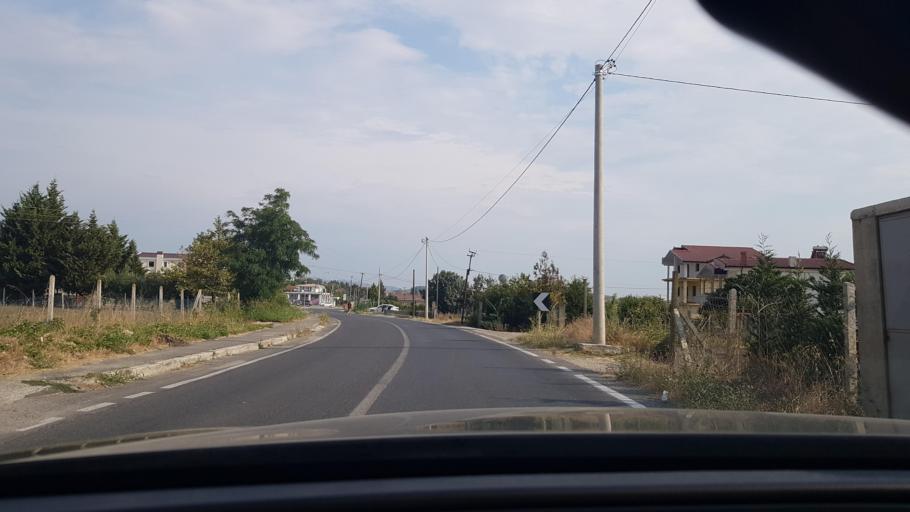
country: AL
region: Durres
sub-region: Rrethi i Durresit
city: Manze
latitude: 41.4647
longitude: 19.5626
